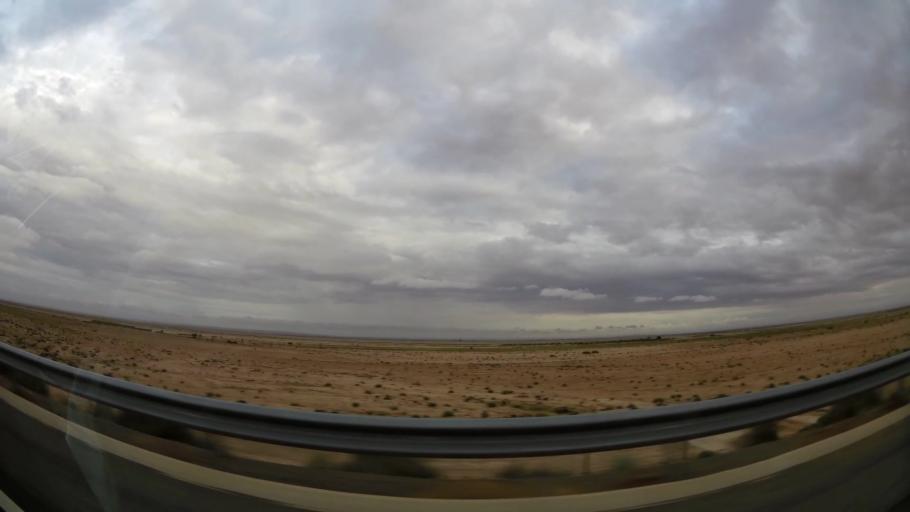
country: MA
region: Taza-Al Hoceima-Taounate
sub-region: Taza
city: Guercif
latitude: 34.3272
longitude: -3.5501
